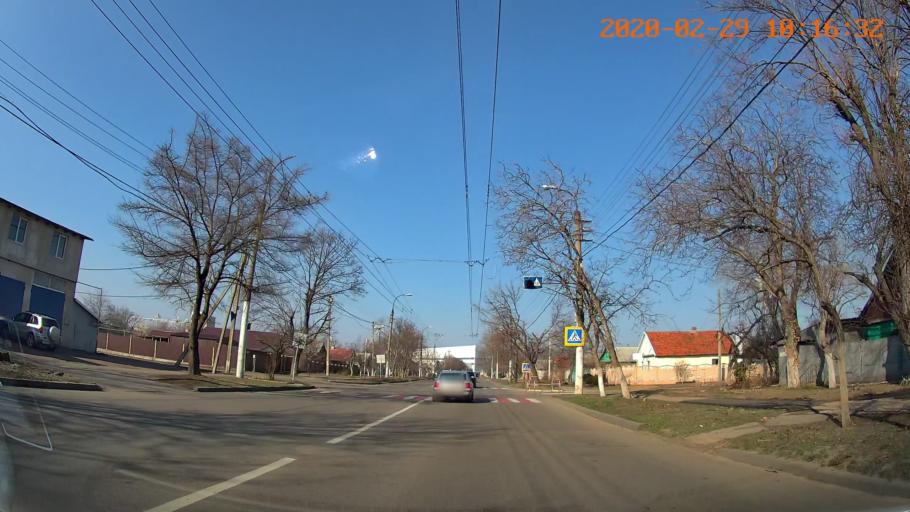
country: MD
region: Telenesti
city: Tiraspolul Nou
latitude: 46.8553
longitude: 29.6279
